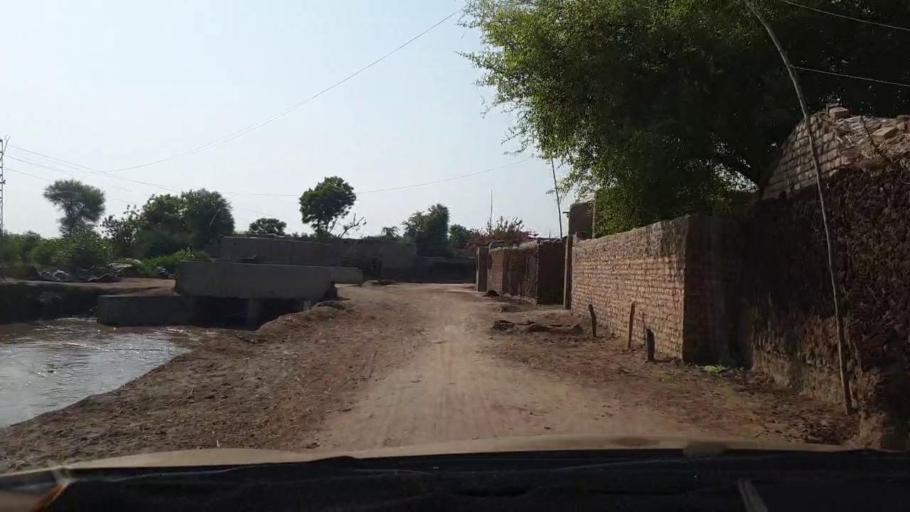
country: PK
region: Sindh
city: Larkana
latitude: 27.6241
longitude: 68.2608
